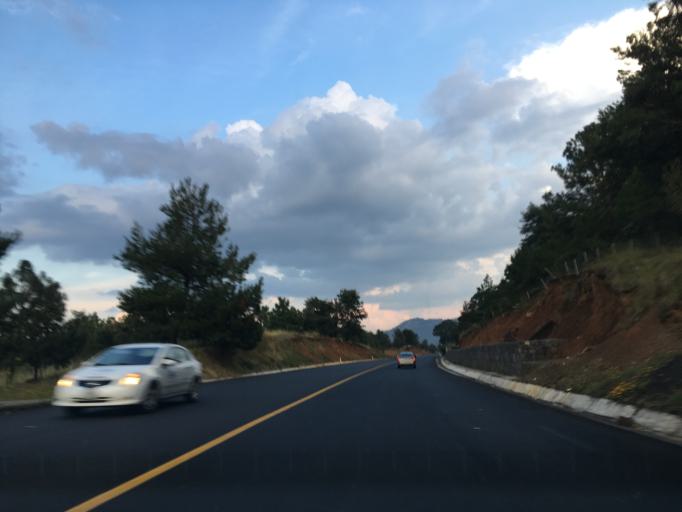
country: MX
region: Michoacan
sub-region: Patzcuaro
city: Santa Ana Chapitiro
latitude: 19.5045
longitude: -101.6886
